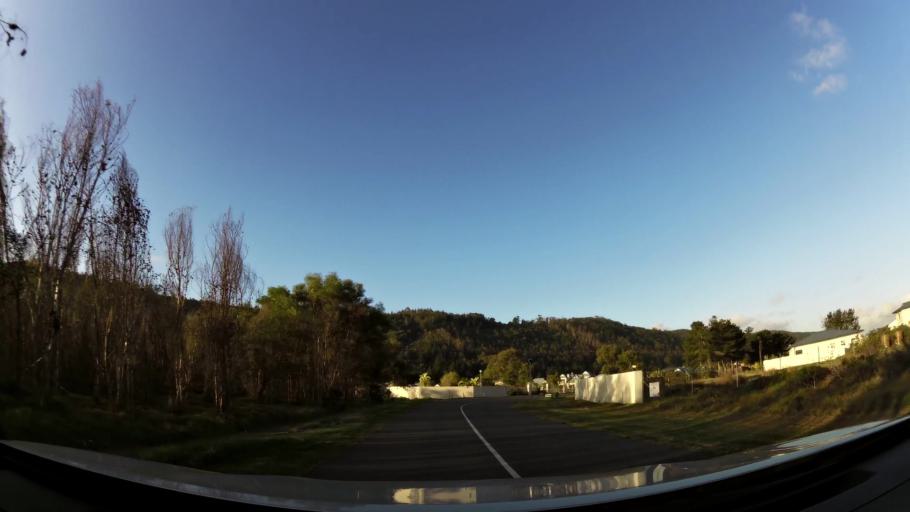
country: ZA
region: Western Cape
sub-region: Eden District Municipality
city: Knysna
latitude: -34.0127
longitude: 22.7902
